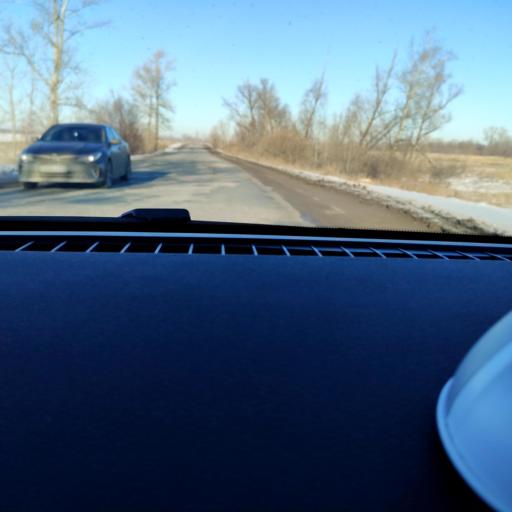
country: RU
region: Samara
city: Spiridonovka
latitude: 53.1199
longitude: 50.6326
